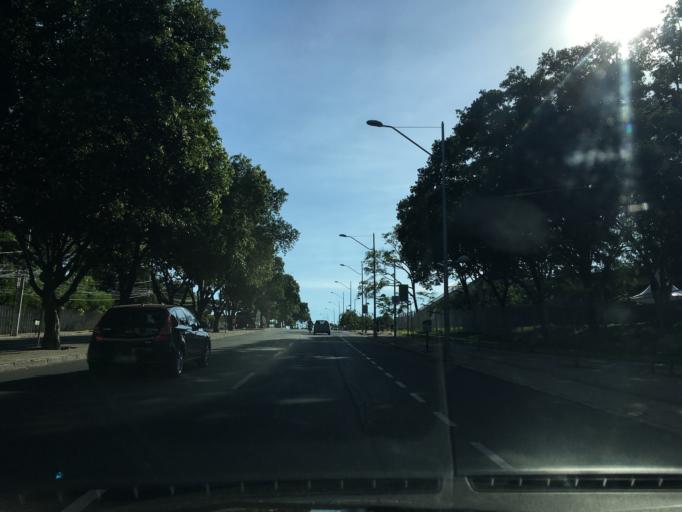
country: BR
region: Minas Gerais
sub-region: Belo Horizonte
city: Belo Horizonte
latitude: -19.8639
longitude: -43.9728
